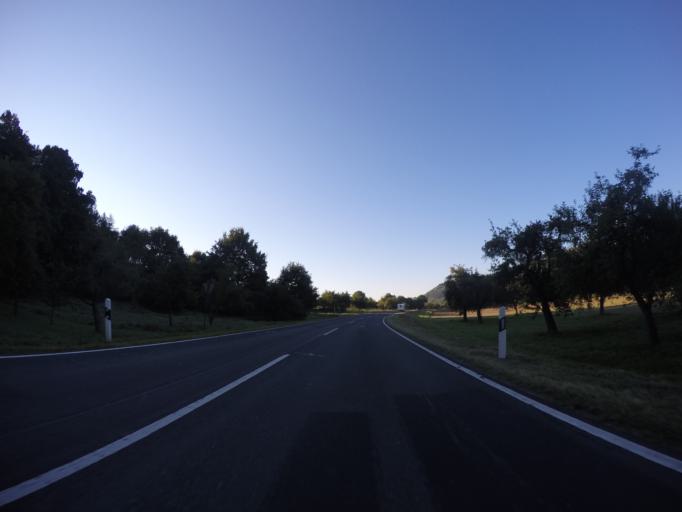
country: DE
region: Bavaria
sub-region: Regierungsbezirk Unterfranken
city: Kreuzwertheim
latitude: 49.7804
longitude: 9.5151
